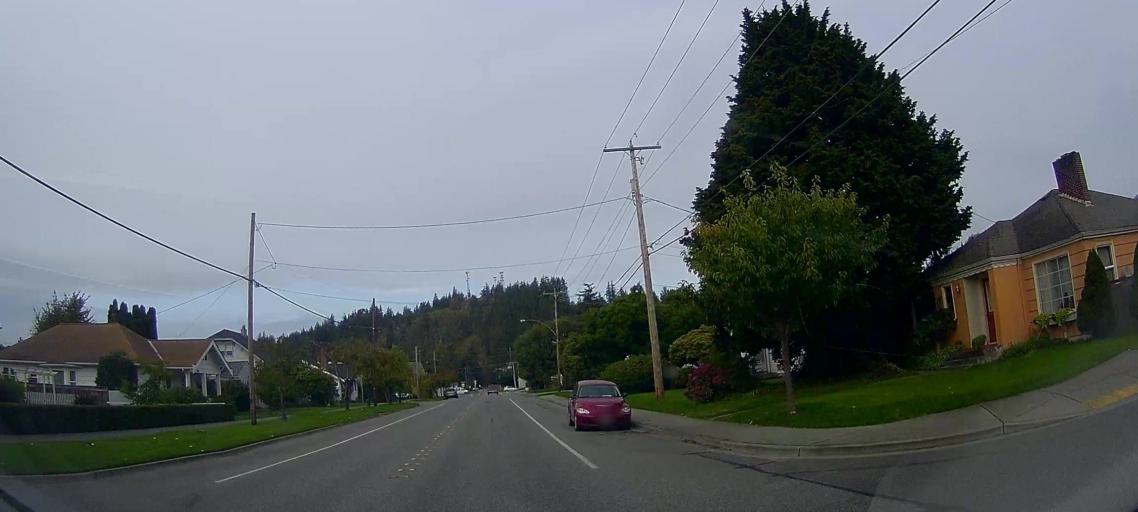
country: US
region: Washington
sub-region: Skagit County
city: Burlington
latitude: 48.4740
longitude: -122.3248
